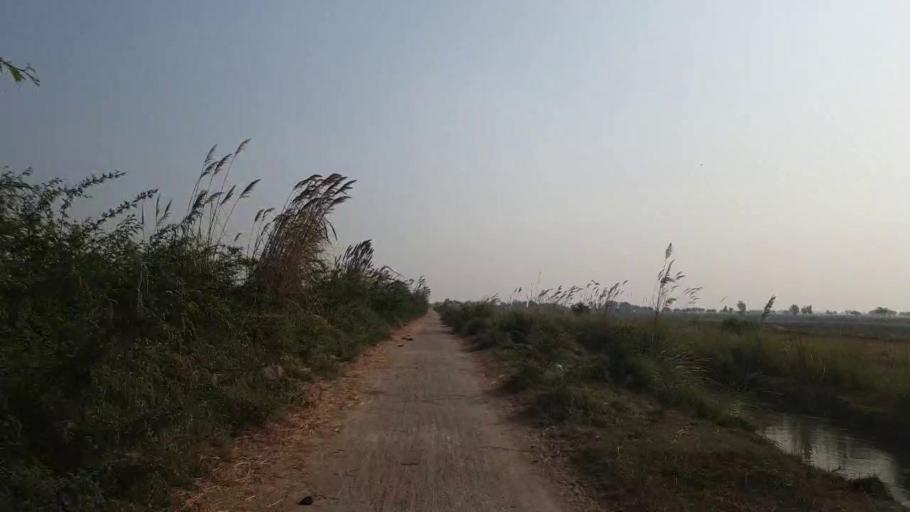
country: PK
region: Sindh
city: Tando Muhammad Khan
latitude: 25.0942
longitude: 68.3560
